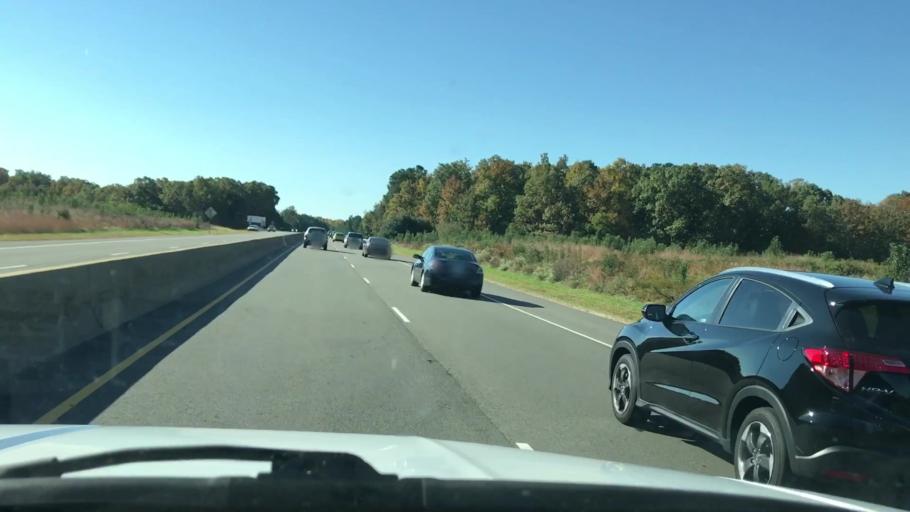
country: US
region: Virginia
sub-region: Henrico County
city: Short Pump
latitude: 37.6380
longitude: -77.5727
